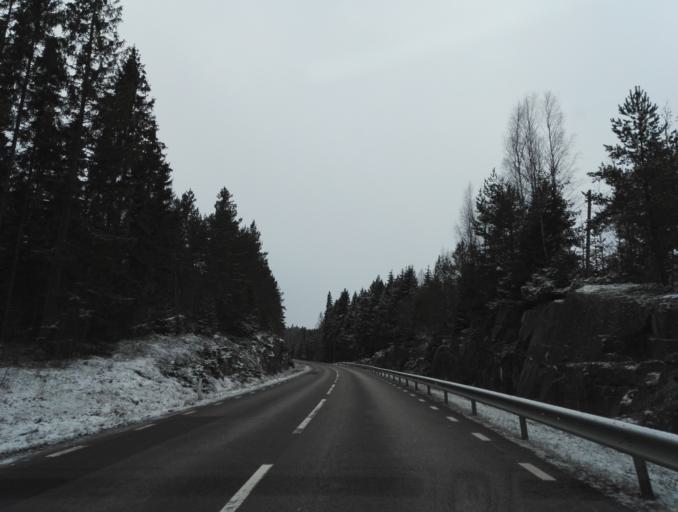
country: SE
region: Kalmar
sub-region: Hultsfreds Kommun
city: Virserum
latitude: 57.1919
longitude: 15.5055
